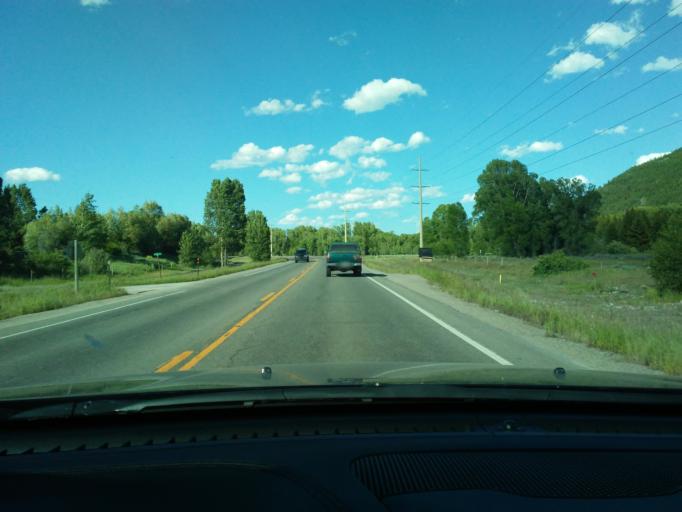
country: US
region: Wyoming
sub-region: Teton County
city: Moose Wilson Road
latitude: 43.5387
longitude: -110.8254
